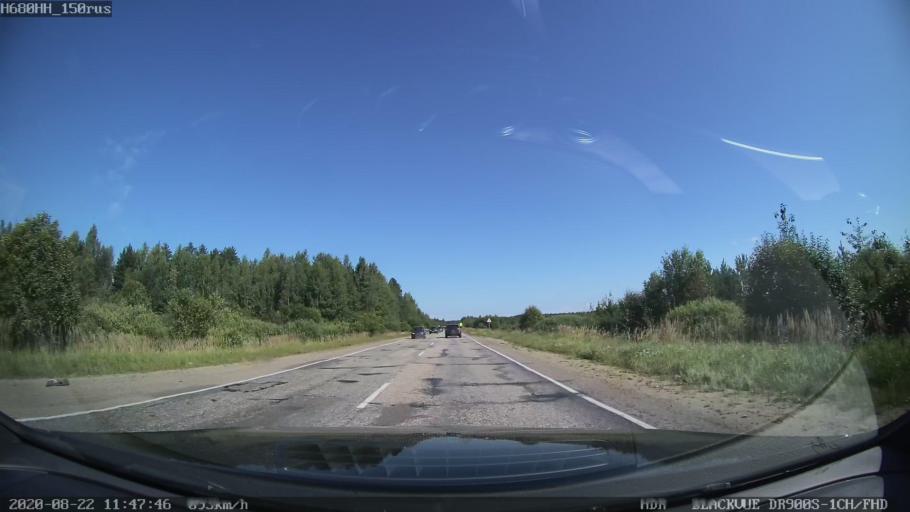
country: RU
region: Tverskaya
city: Sakharovo
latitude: 57.0559
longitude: 36.0925
